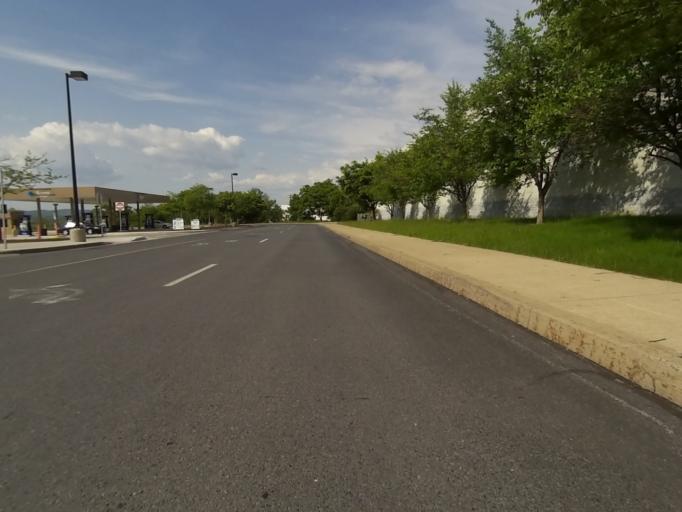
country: US
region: Pennsylvania
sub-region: Centre County
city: Houserville
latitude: 40.8329
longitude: -77.8055
